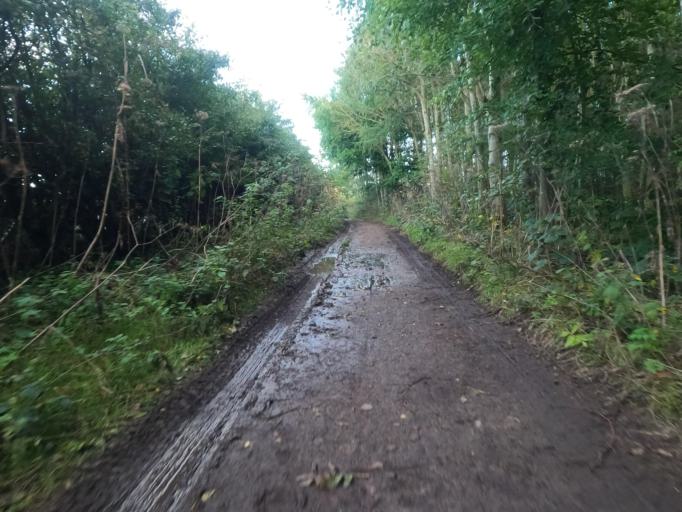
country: GB
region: England
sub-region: Northumberland
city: Seghill
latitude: 55.0690
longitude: -1.5453
